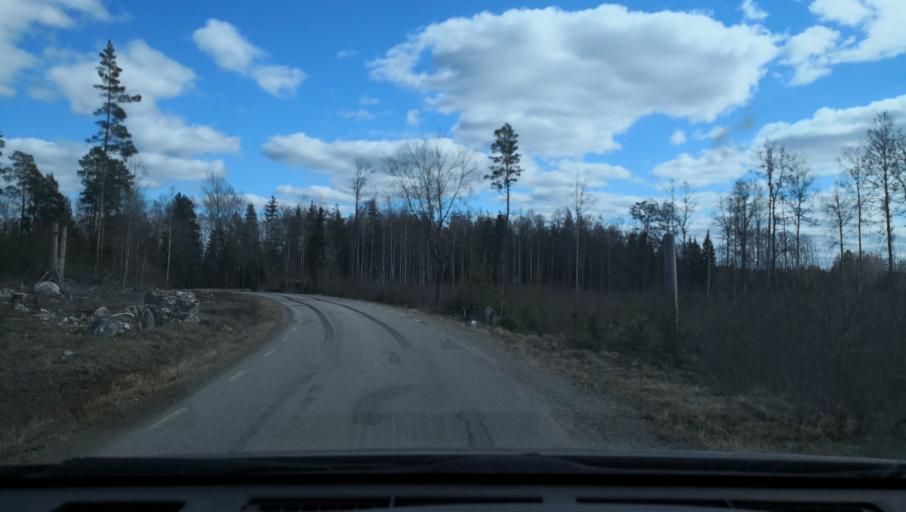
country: SE
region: Vaestmanland
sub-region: Sala Kommun
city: Sala
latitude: 59.8659
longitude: 16.5634
